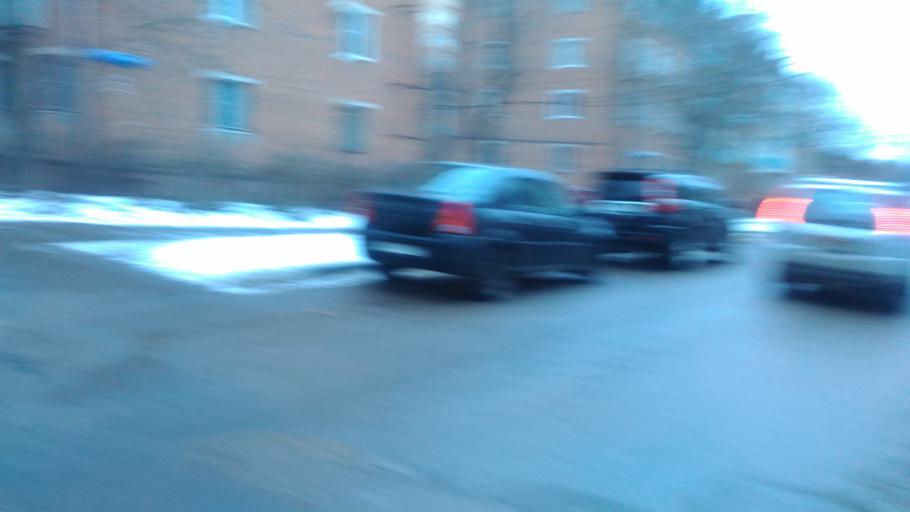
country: RU
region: Tula
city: Tula
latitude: 54.1782
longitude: 37.6043
